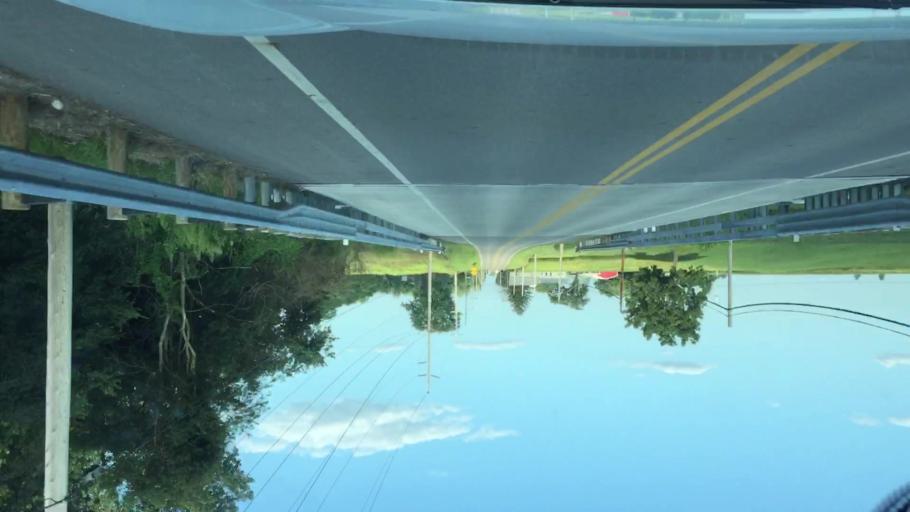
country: US
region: Ohio
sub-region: Clark County
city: Northridge
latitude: 39.9389
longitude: -83.7147
